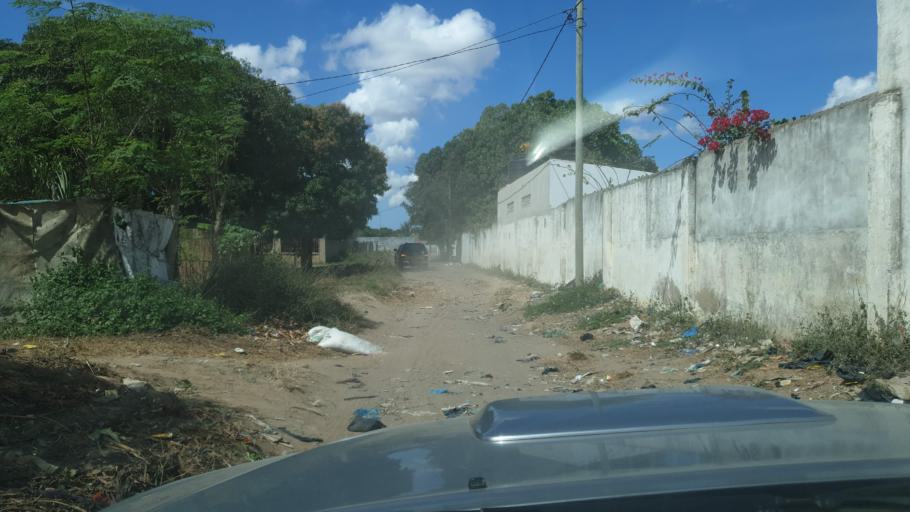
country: MZ
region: Nampula
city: Nacala
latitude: -14.5672
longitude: 40.7009
